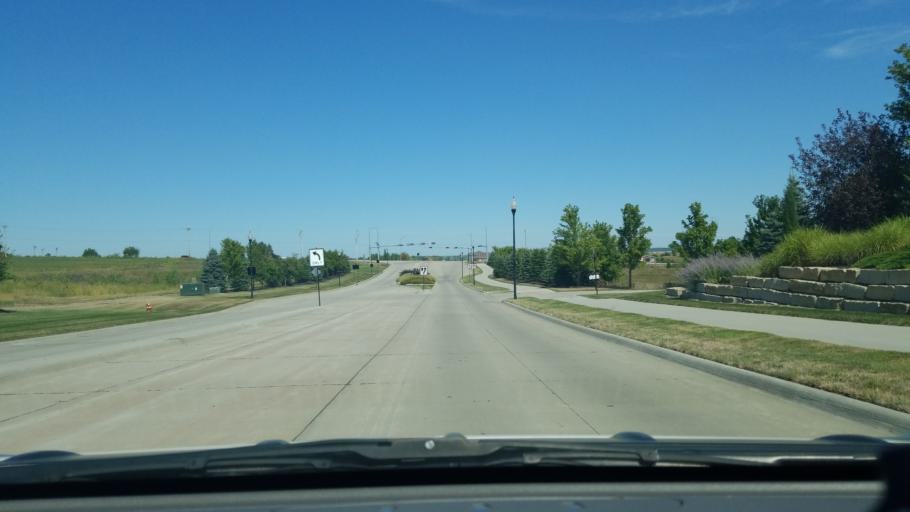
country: US
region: Nebraska
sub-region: Sarpy County
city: Papillion
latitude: 41.1454
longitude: -96.1008
